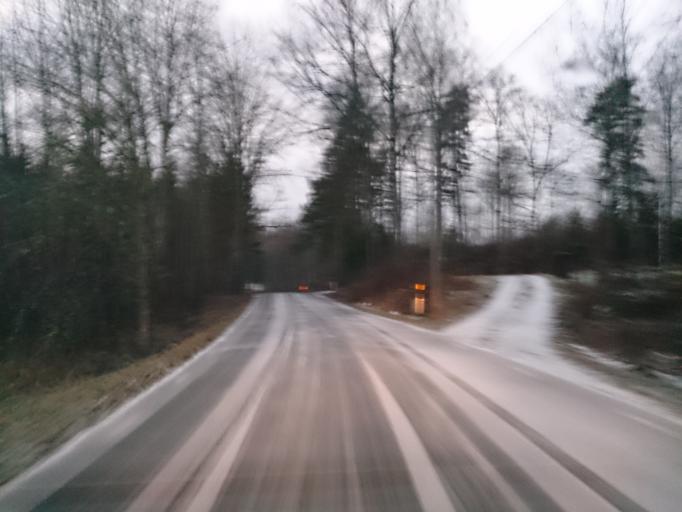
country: SE
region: OEstergoetland
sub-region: Atvidabergs Kommun
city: Atvidaberg
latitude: 58.2779
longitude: 16.1710
